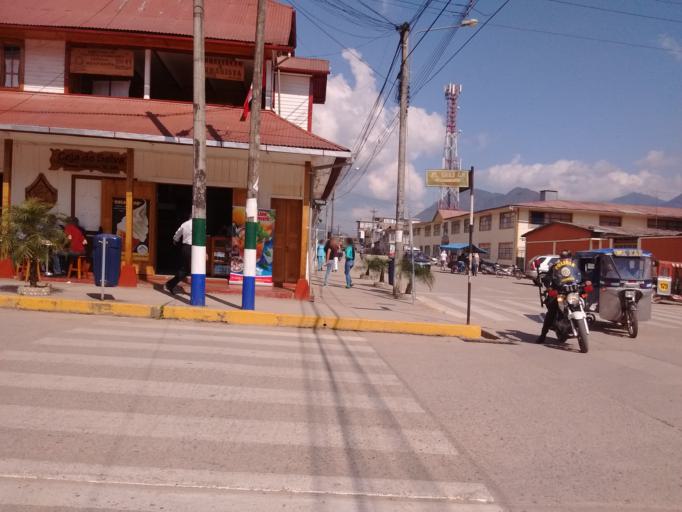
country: PE
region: Pasco
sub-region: Provincia de Oxapampa
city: Oxapampa
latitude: -10.5745
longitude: -75.4039
